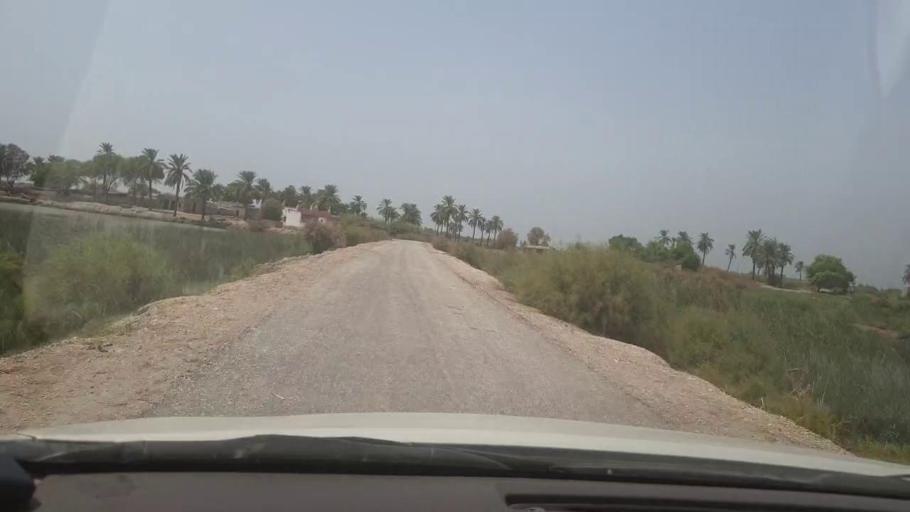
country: PK
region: Sindh
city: Garhi Yasin
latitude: 27.9794
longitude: 68.5443
